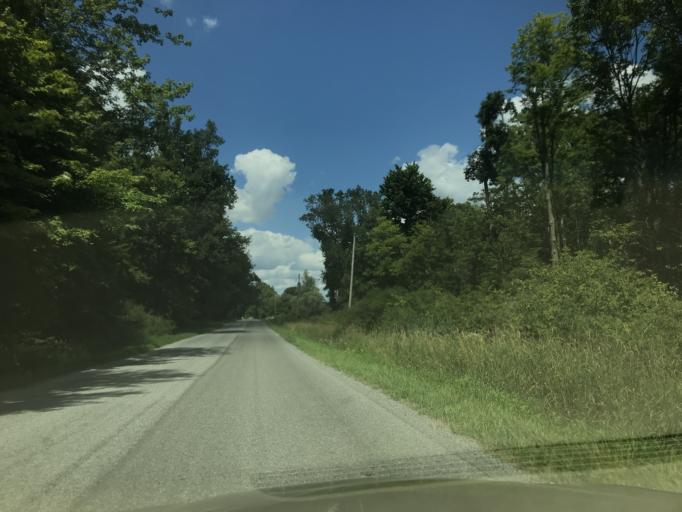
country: US
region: Michigan
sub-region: Ingham County
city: Holt
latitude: 42.6194
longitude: -84.5626
